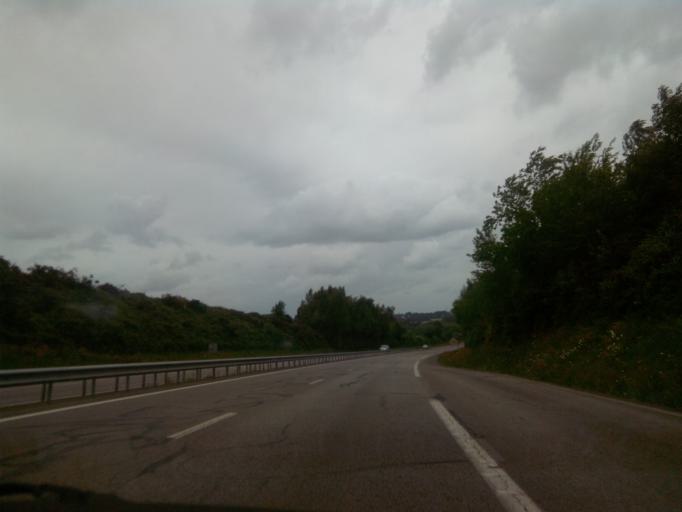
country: FR
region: Brittany
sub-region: Departement du Morbihan
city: Malestroit
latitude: 47.8263
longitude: -2.4334
